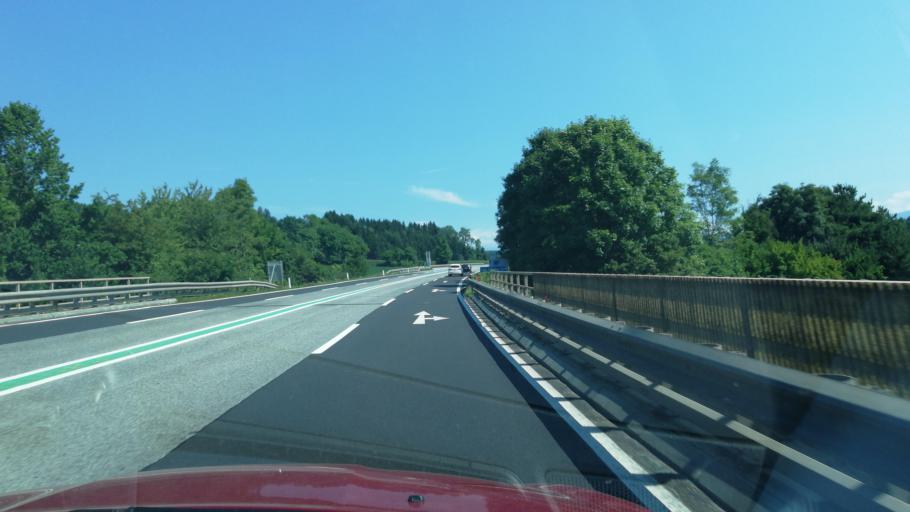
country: AT
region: Carinthia
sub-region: Politischer Bezirk Sankt Veit an der Glan
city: Sankt Veit an der Glan
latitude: 46.7905
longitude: 14.3863
